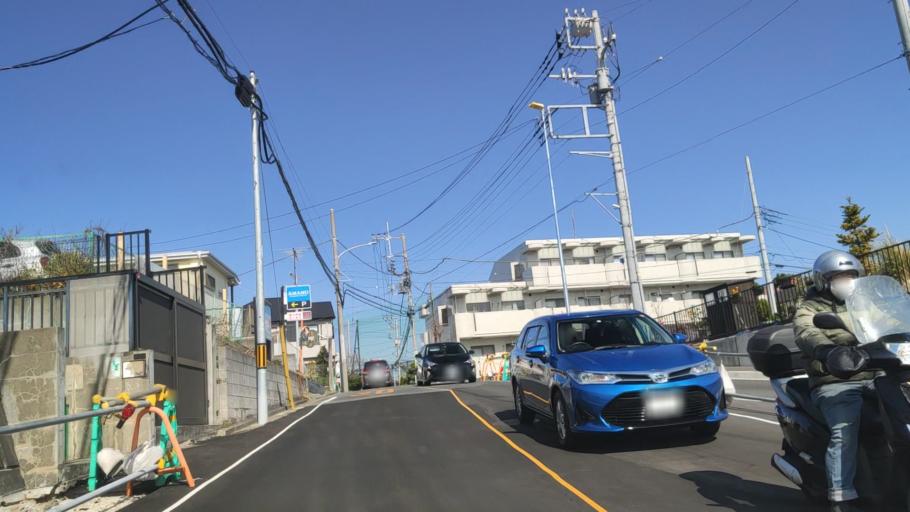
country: JP
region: Kanagawa
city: Yokohama
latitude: 35.5087
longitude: 139.6397
